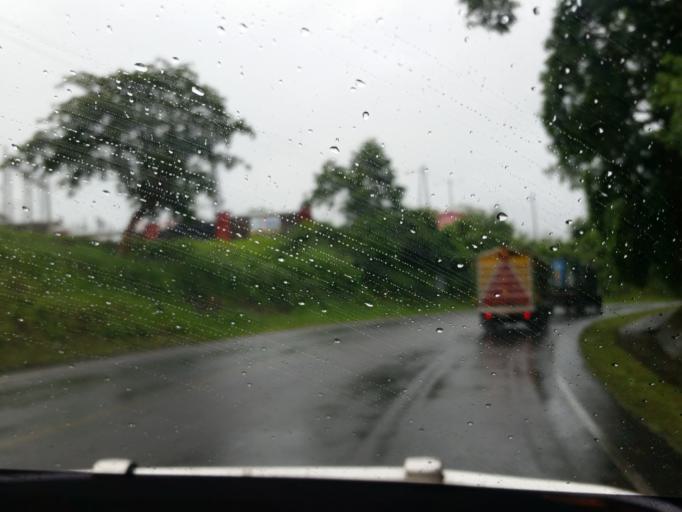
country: NI
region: Matagalpa
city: Matagalpa
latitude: 12.9106
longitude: -85.9561
